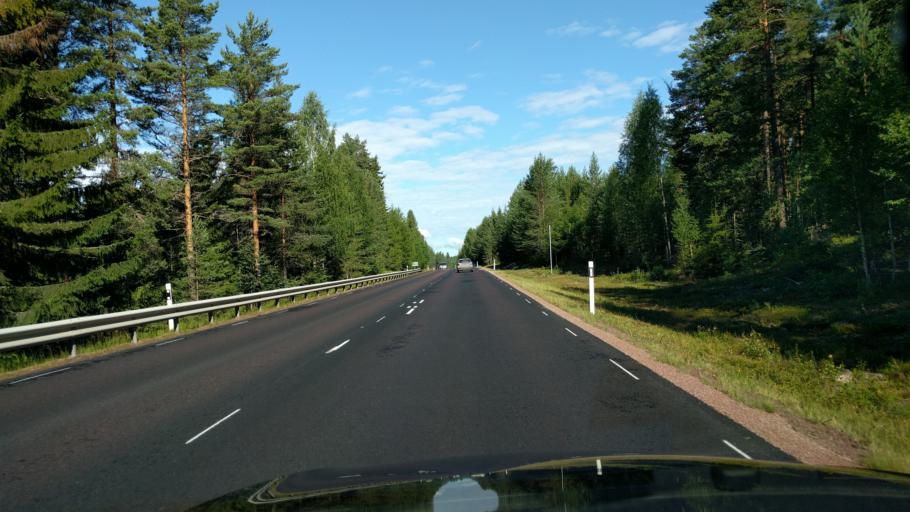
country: SE
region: Dalarna
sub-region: Alvdalens Kommun
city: AElvdalen
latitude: 61.1313
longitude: 14.1810
